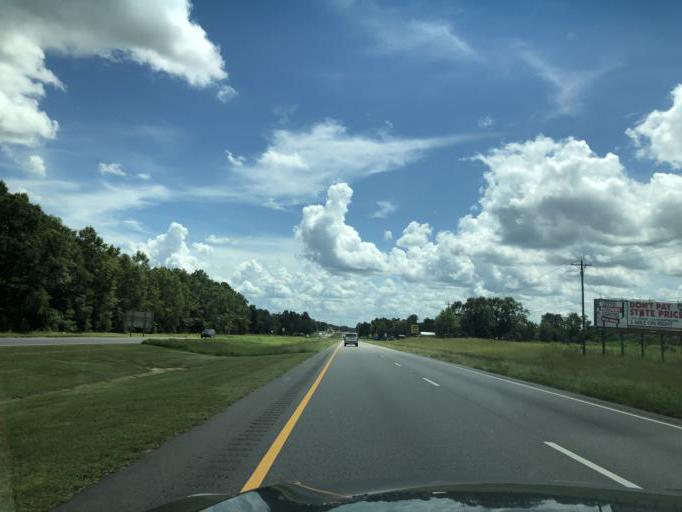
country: US
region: Alabama
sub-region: Houston County
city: Cottonwood
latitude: 31.0071
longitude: -85.4080
